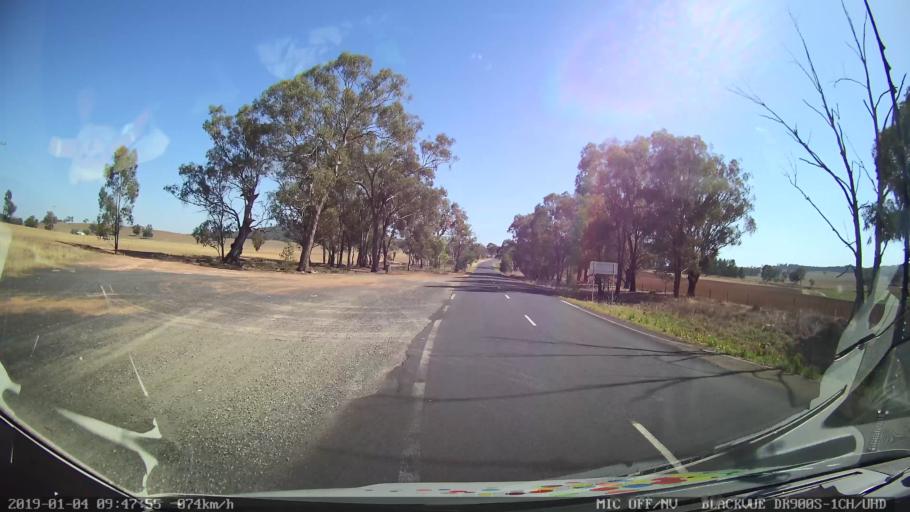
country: AU
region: New South Wales
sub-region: Cabonne
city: Canowindra
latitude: -33.6015
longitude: 148.4319
